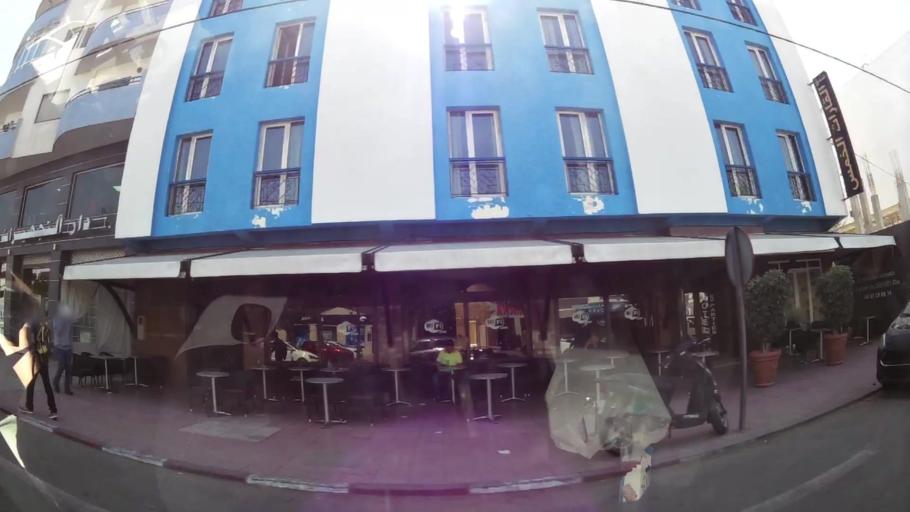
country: MA
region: Souss-Massa-Draa
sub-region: Agadir-Ida-ou-Tnan
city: Agadir
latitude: 30.4110
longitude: -9.5905
